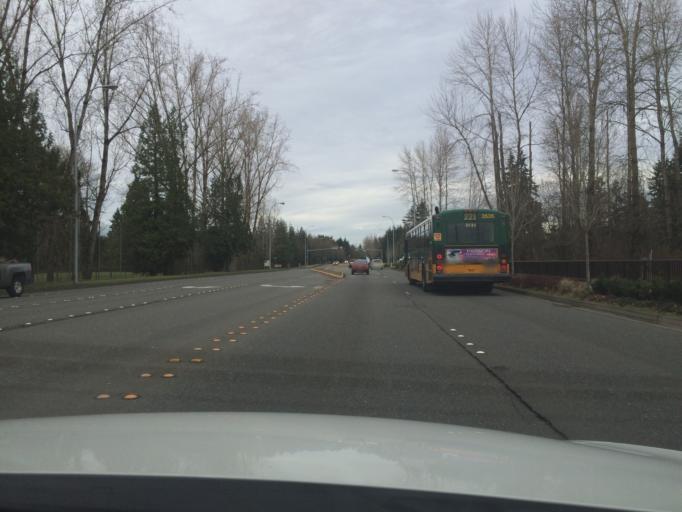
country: US
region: Washington
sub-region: King County
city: Redmond
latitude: 47.6557
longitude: -122.1432
